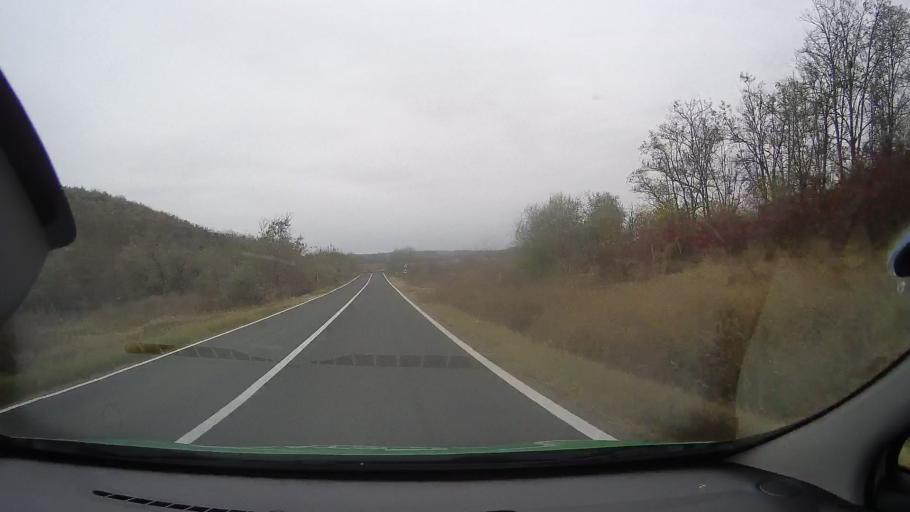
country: RO
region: Constanta
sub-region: Comuna Garliciu
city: Garliciu
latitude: 44.7067
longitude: 28.0685
